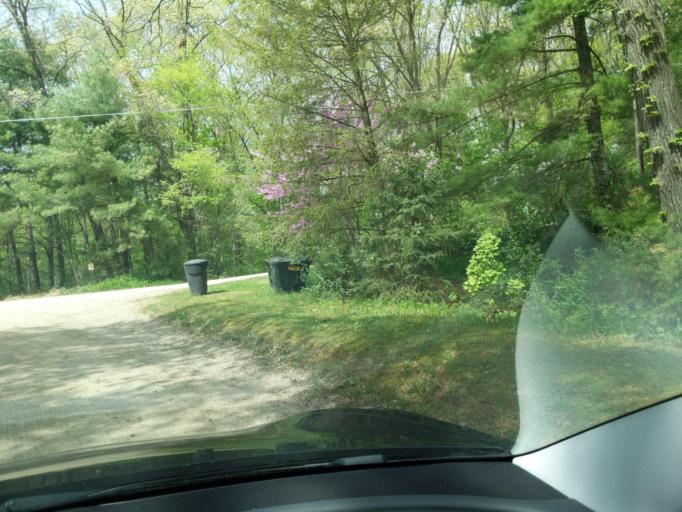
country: US
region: Michigan
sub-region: Ingham County
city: Stockbridge
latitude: 42.4255
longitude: -84.0709
